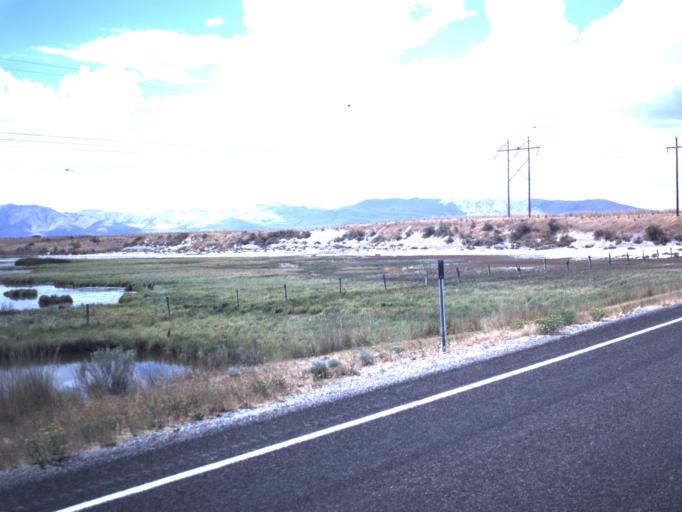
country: US
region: Utah
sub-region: Box Elder County
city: Tremonton
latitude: 41.6036
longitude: -112.3132
